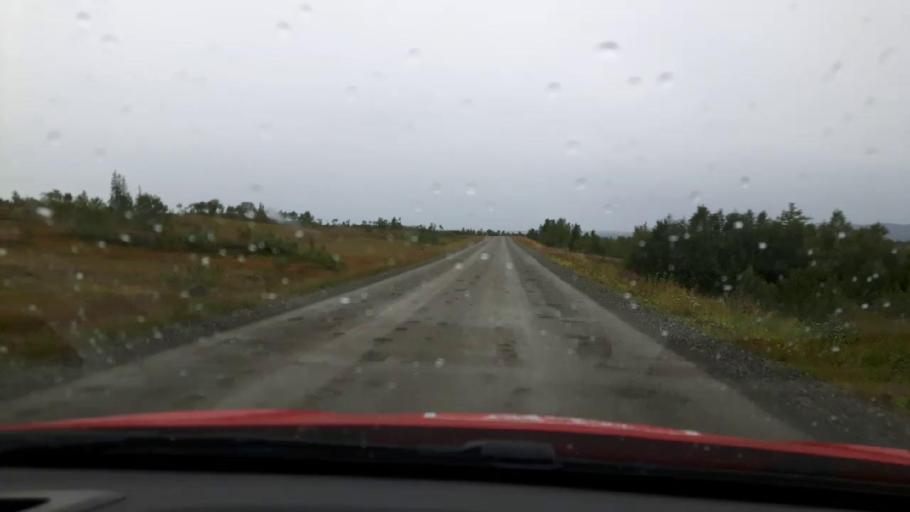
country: NO
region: Nord-Trondelag
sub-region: Meraker
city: Meraker
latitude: 63.6097
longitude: 12.2760
